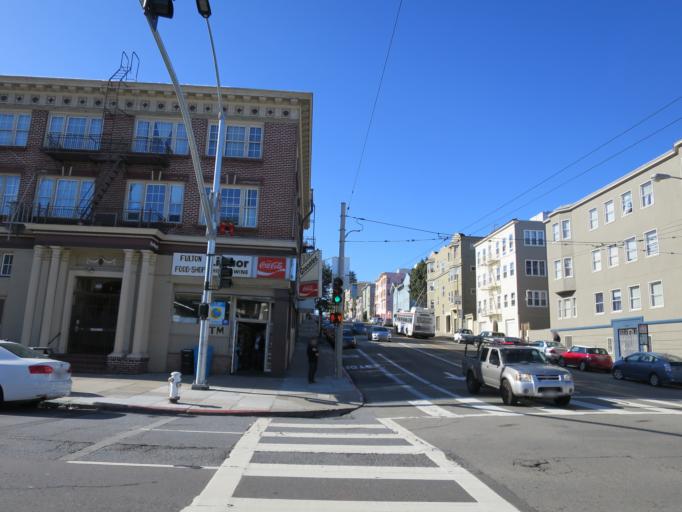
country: US
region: California
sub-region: San Francisco County
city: San Francisco
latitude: 37.7757
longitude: -122.4464
